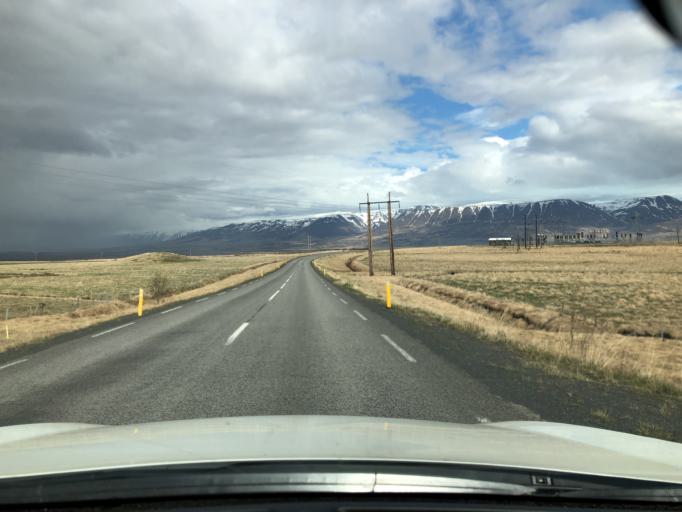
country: IS
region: Northwest
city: Saudarkrokur
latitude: 65.5459
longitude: -19.4938
